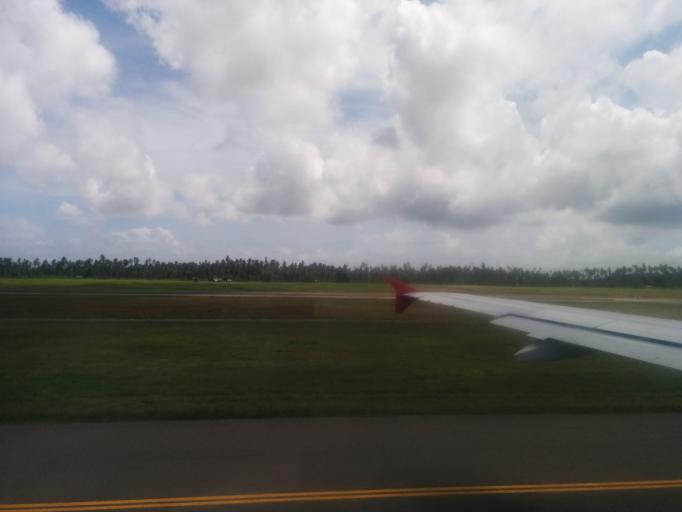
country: LK
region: Western
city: Katunayaka
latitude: 7.1845
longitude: 79.8886
